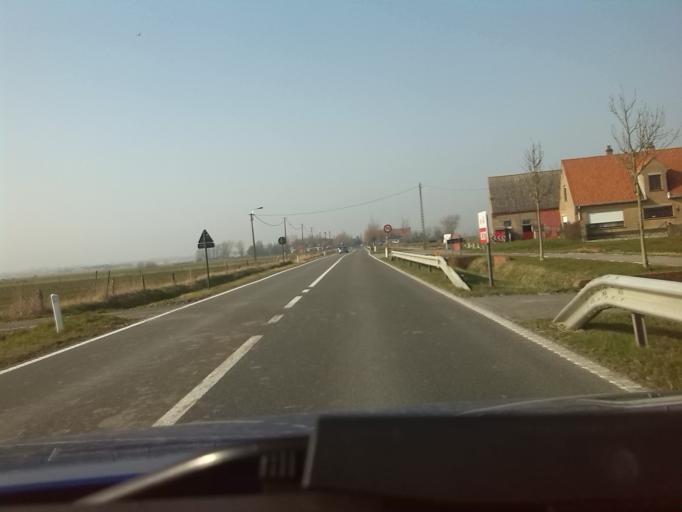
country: BE
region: Flanders
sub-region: Provincie West-Vlaanderen
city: Wenduine
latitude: 51.2706
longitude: 3.0934
